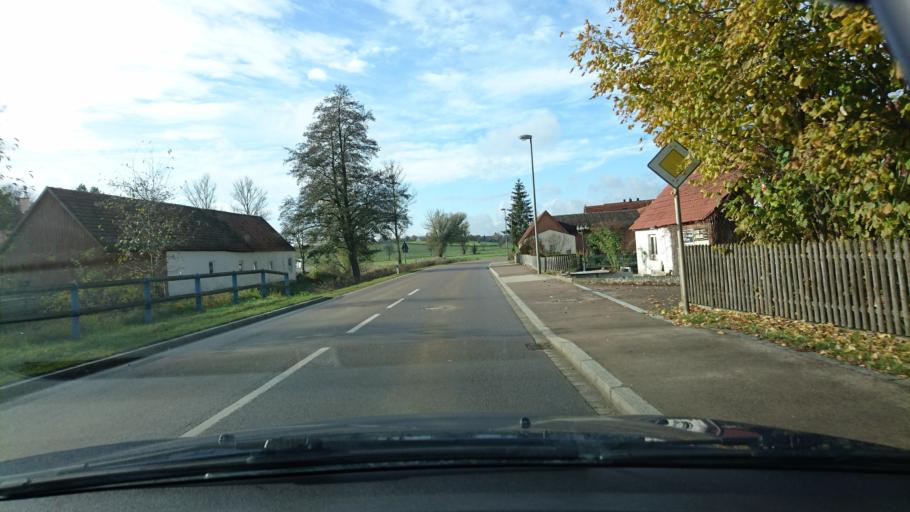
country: DE
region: Bavaria
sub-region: Swabia
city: Amerdingen
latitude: 48.7267
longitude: 10.5354
